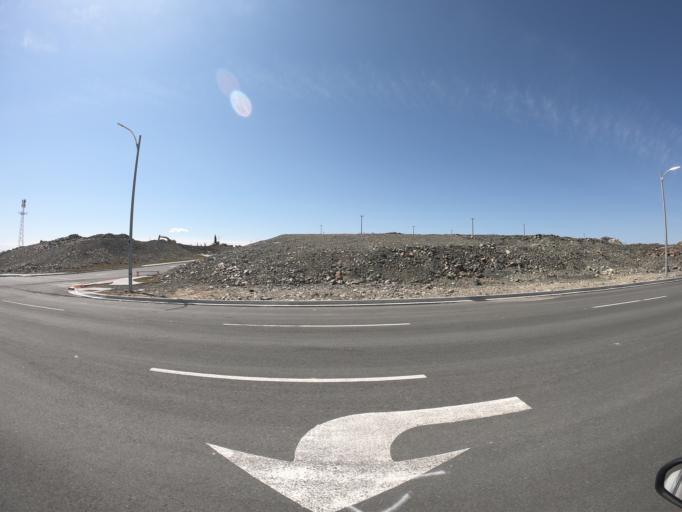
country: CA
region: Newfoundland and Labrador
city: Mount Pearl
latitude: 47.5089
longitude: -52.8329
